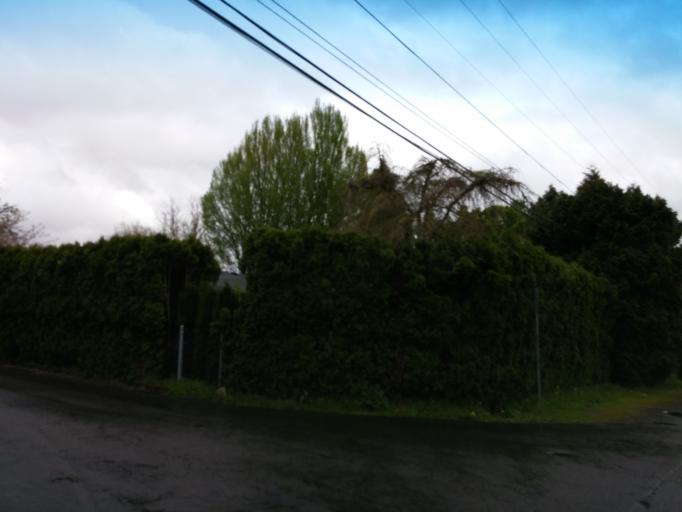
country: US
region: Oregon
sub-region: Washington County
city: Cedar Mill
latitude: 45.5174
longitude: -122.8267
